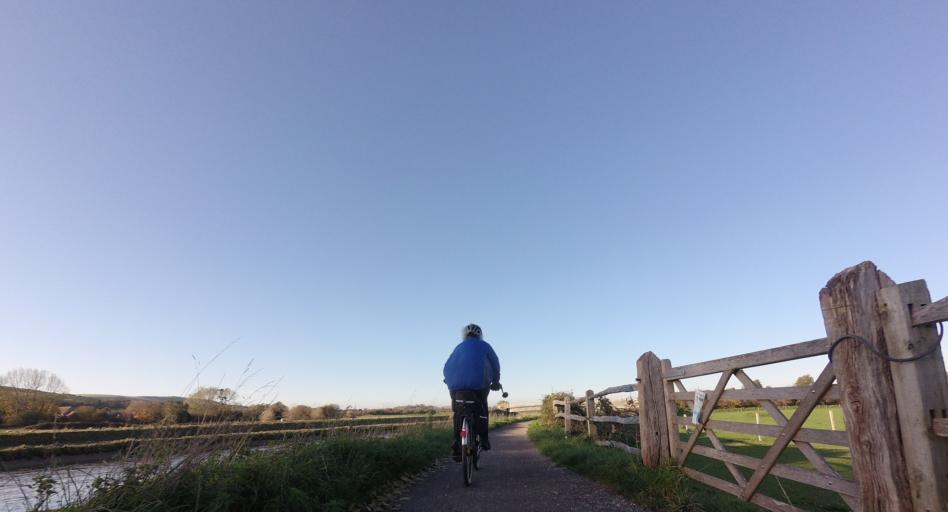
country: GB
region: England
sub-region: West Sussex
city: Steyning
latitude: 50.8697
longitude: -0.3007
